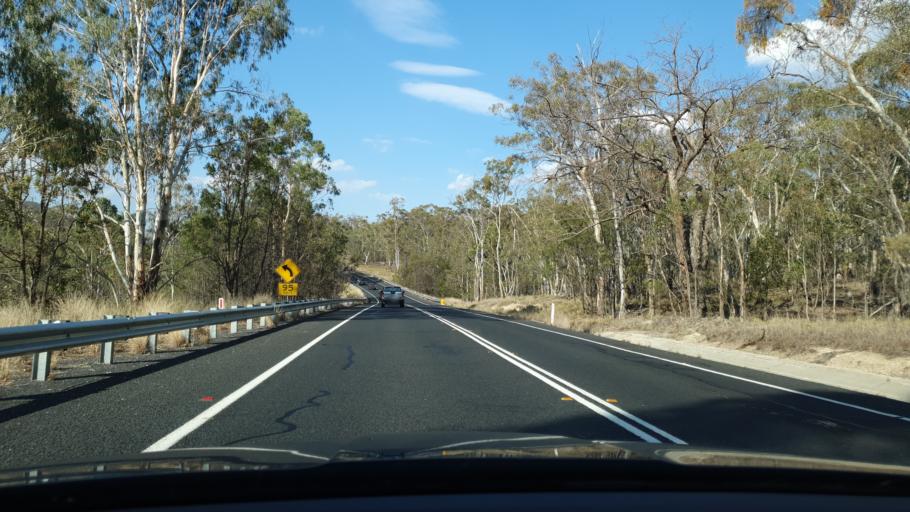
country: AU
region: New South Wales
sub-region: Tenterfield Municipality
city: Carrolls Creek
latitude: -29.2635
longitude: 151.9862
